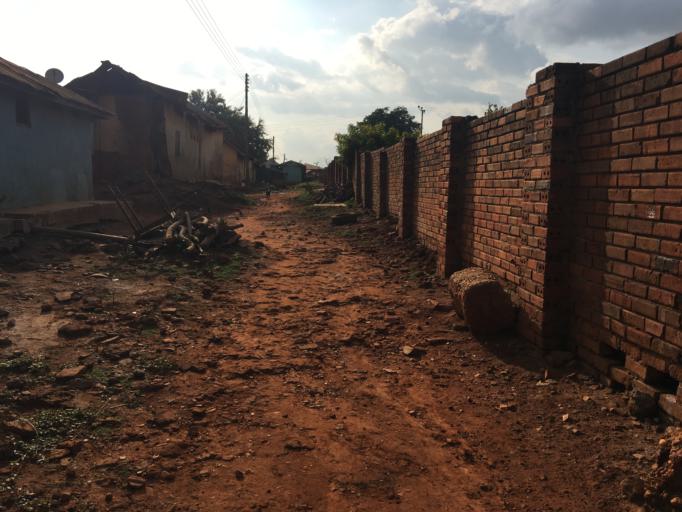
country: GH
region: Western
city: Bibiani
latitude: 6.8044
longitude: -2.5207
